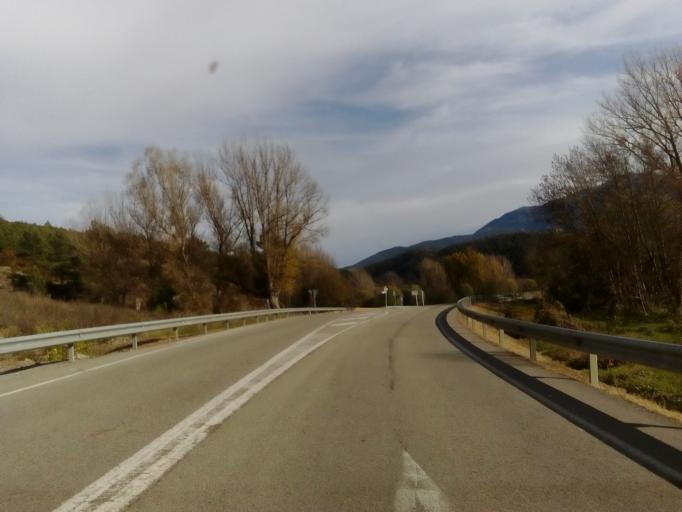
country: ES
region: Catalonia
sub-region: Provincia de Lleida
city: Bellver de Cerdanya
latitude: 42.3736
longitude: 1.7875
